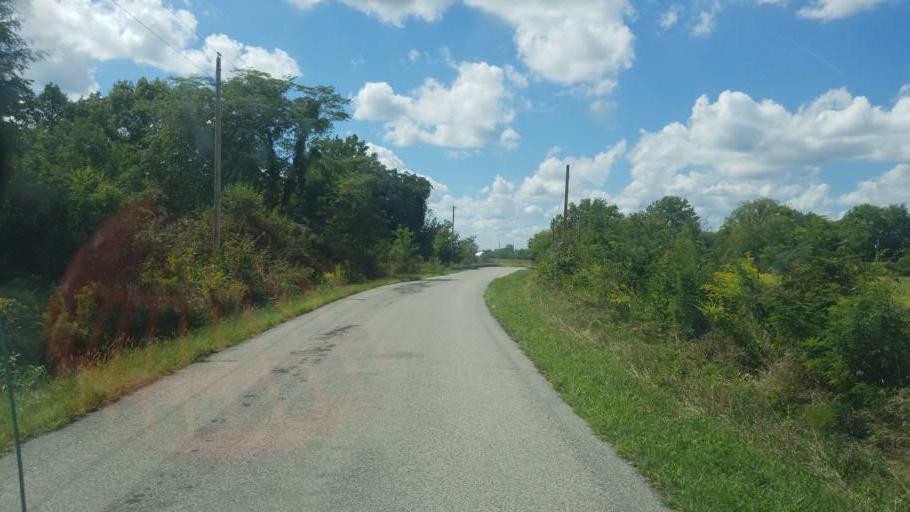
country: US
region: Ohio
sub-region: Marion County
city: Prospect
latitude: 40.3723
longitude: -83.1927
